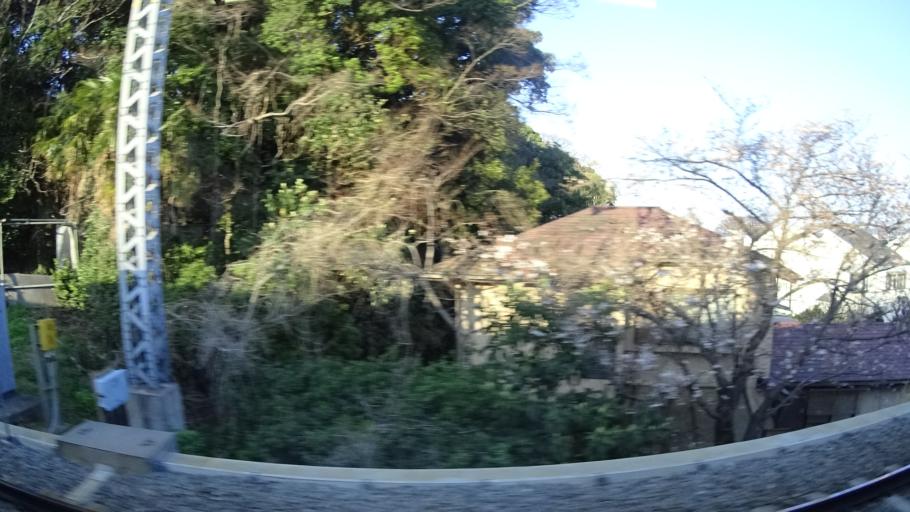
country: JP
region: Kanagawa
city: Yokosuka
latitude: 35.2645
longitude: 139.6845
